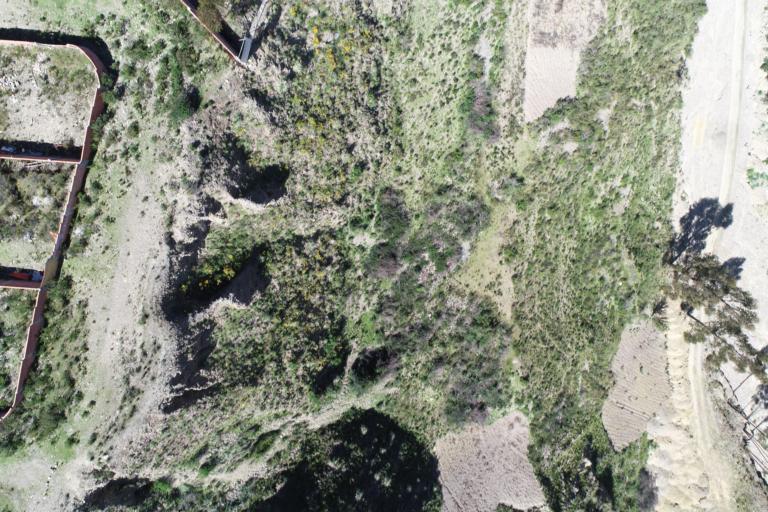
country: BO
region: La Paz
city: La Paz
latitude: -16.5030
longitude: -68.0591
